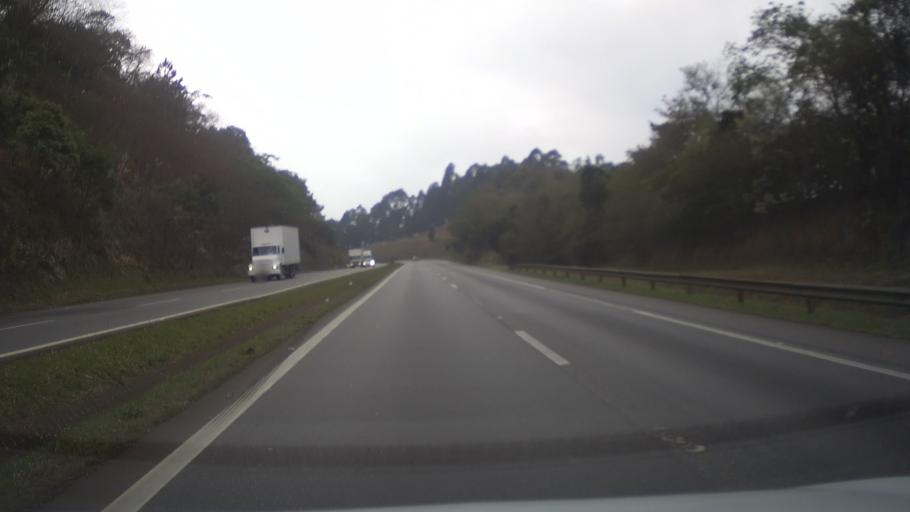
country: BR
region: Minas Gerais
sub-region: Extrema
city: Extrema
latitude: -22.8597
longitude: -46.3409
